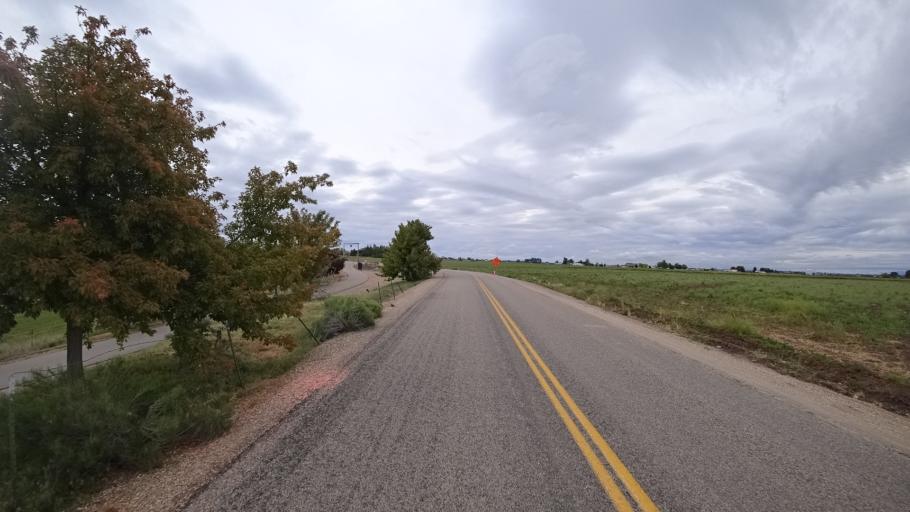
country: US
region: Idaho
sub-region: Ada County
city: Star
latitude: 43.6707
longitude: -116.5095
